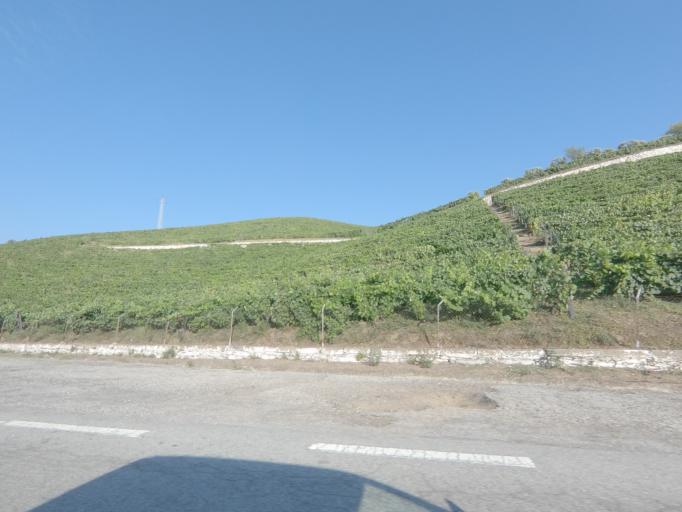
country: PT
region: Viseu
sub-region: Armamar
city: Armamar
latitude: 41.1444
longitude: -7.6890
